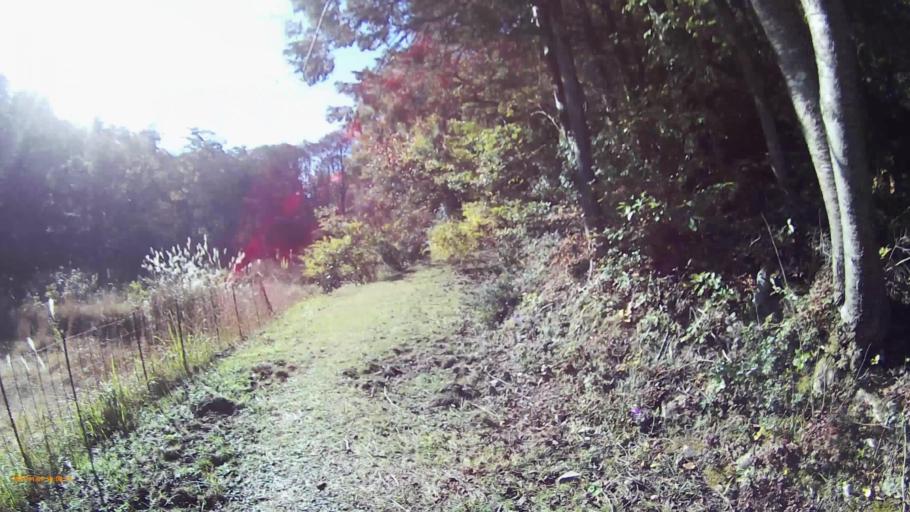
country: JP
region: Gifu
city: Mizunami
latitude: 35.4404
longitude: 137.3271
